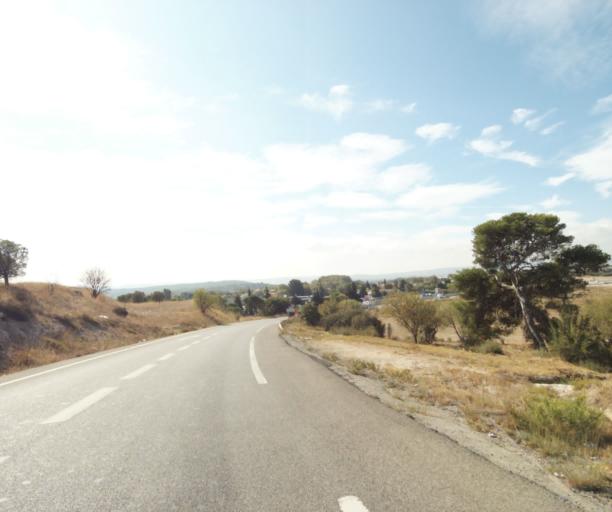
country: FR
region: Provence-Alpes-Cote d'Azur
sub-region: Departement des Bouches-du-Rhone
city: Saint-Victoret
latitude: 43.4257
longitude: 5.2351
